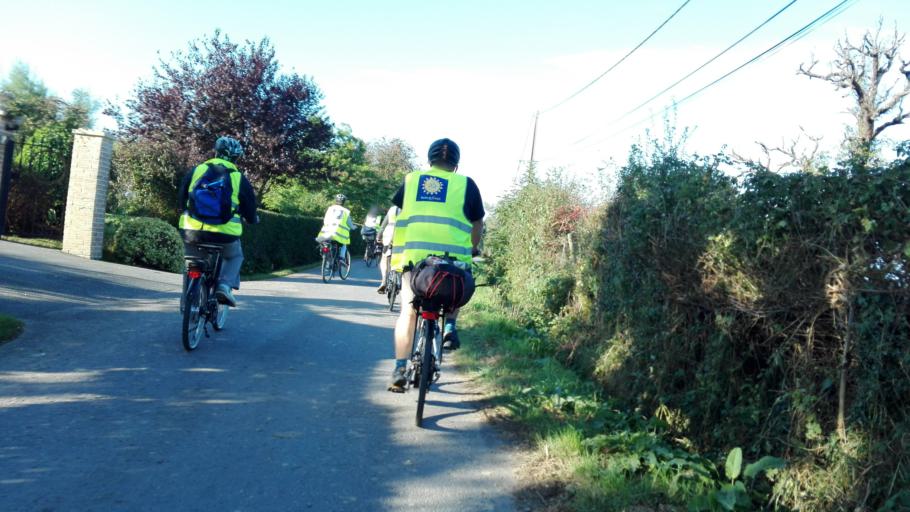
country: FR
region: Nord-Pas-de-Calais
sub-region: Departement du Pas-de-Calais
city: Eperlecques
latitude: 50.8189
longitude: 2.1596
